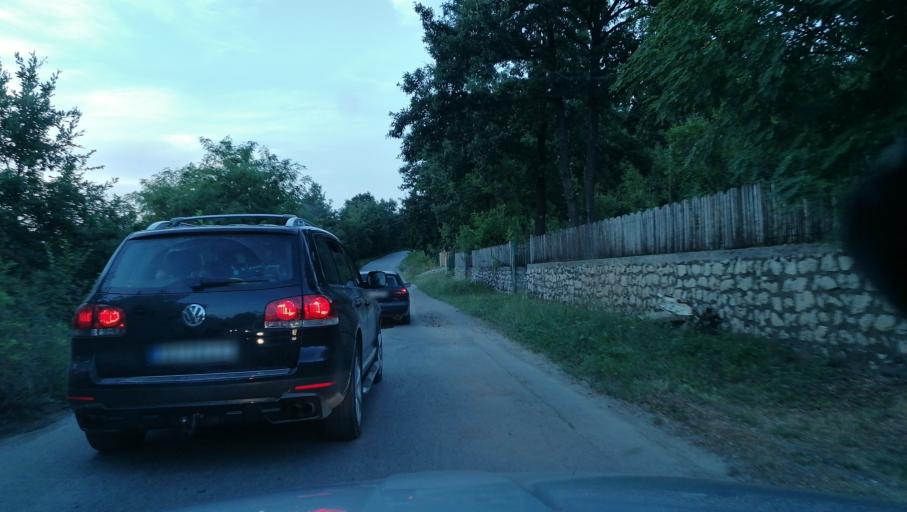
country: RS
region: Central Serbia
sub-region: Kolubarski Okrug
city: Valjevo
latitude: 44.2391
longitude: 19.8603
